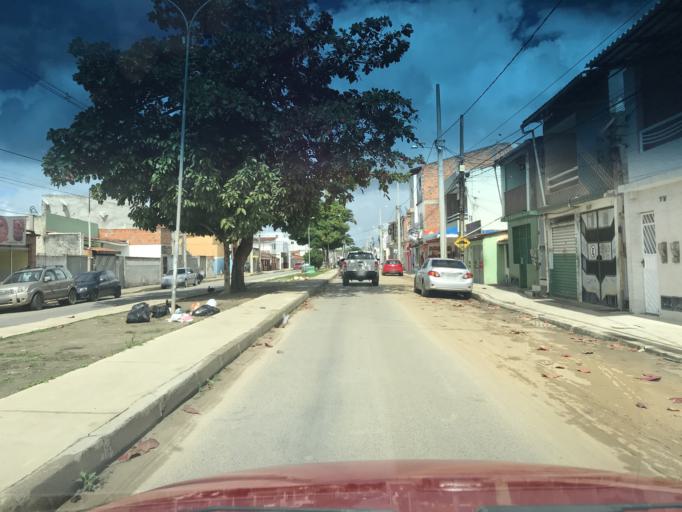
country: BR
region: Bahia
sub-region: Santo Antonio De Jesus
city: Santo Antonio de Jesus
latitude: -12.9755
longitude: -39.2743
